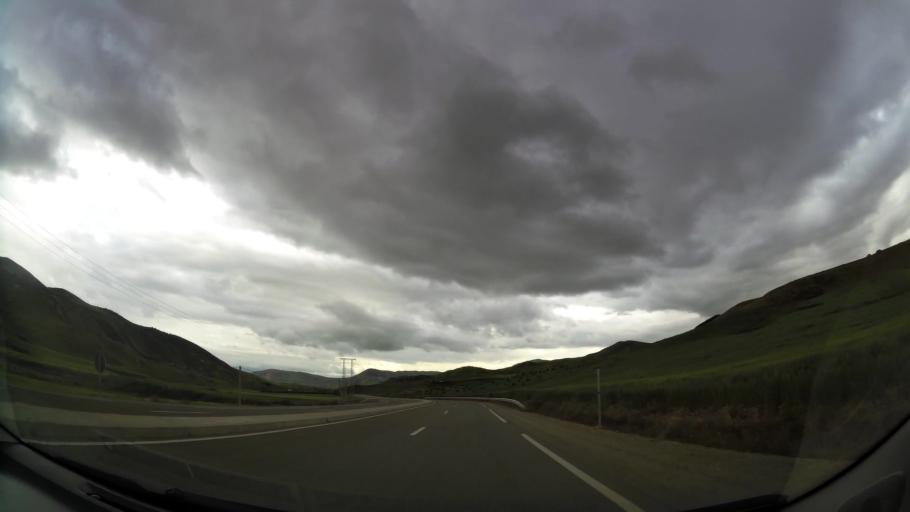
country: MA
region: Taza-Al Hoceima-Taounate
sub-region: Taza
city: Taza
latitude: 34.3355
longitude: -3.9428
